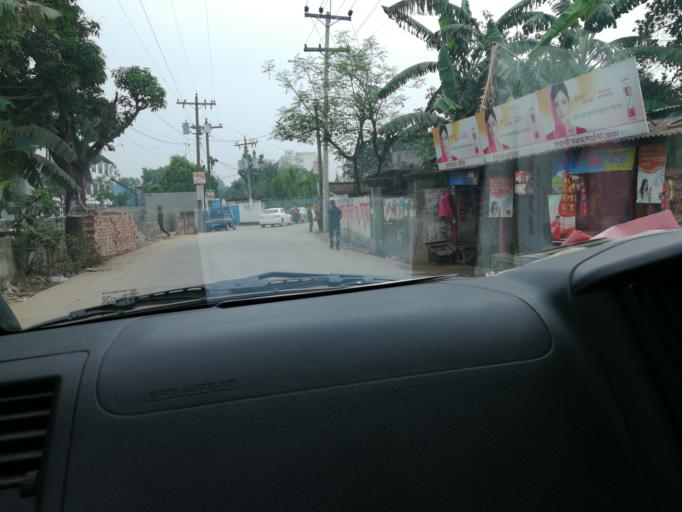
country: BD
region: Dhaka
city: Tungi
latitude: 23.8812
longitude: 90.3098
